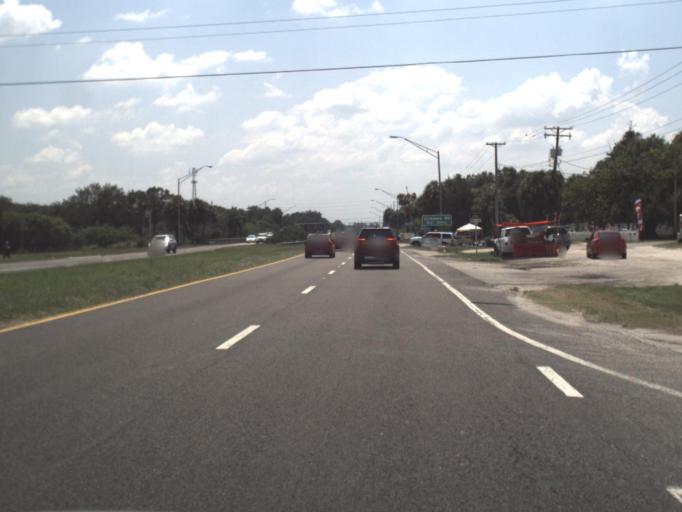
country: US
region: Florida
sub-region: Hillsborough County
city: Gibsonton
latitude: 27.8398
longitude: -82.3818
